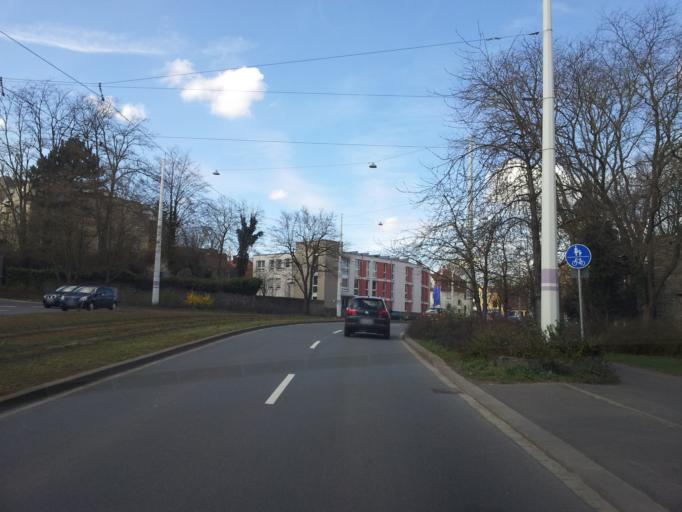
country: DE
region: Bavaria
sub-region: Regierungsbezirk Unterfranken
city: Wuerzburg
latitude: 49.7630
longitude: 9.9448
